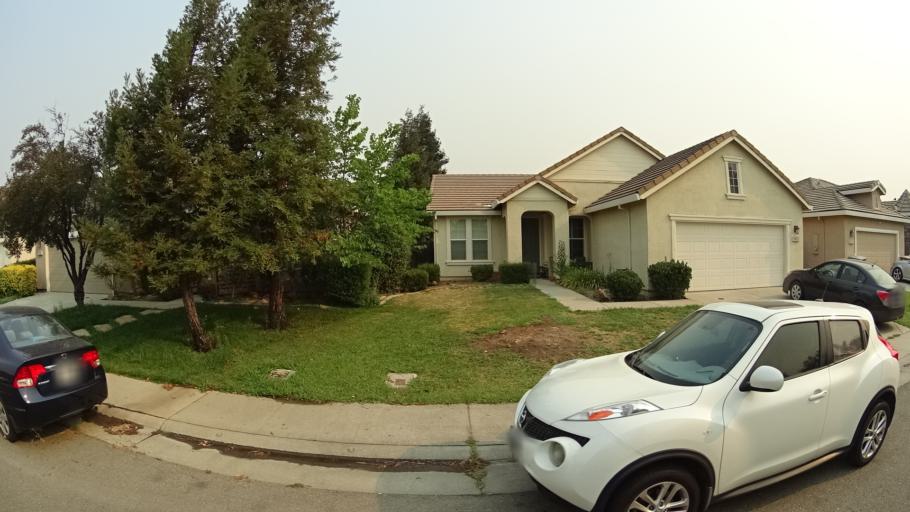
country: US
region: California
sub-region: Sacramento County
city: Laguna
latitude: 38.4010
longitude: -121.4480
